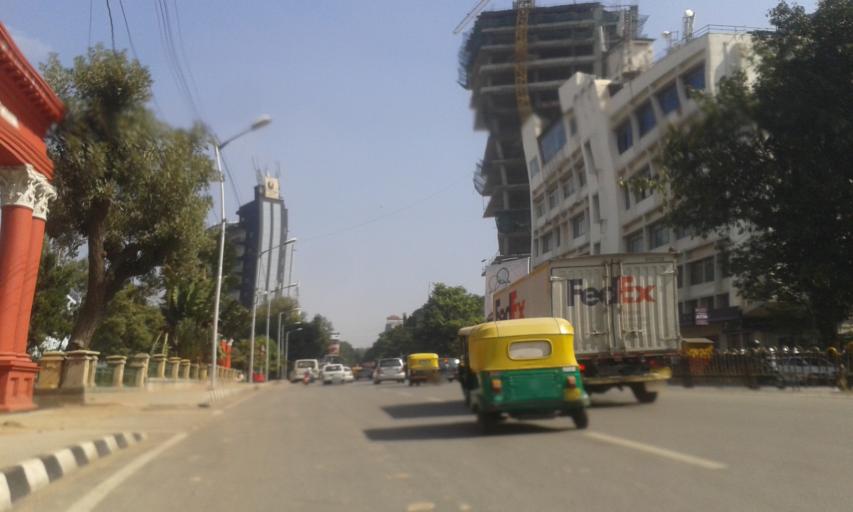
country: IN
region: Karnataka
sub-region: Bangalore Urban
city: Bangalore
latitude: 12.9741
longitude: 77.5959
